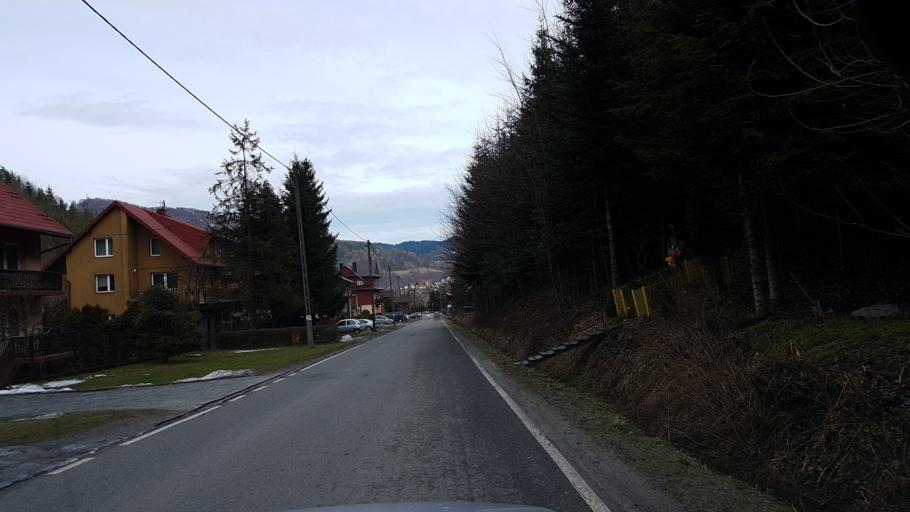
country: PL
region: Lesser Poland Voivodeship
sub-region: Powiat nowosadecki
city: Piwniczna-Zdroj
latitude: 49.4350
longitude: 20.7008
